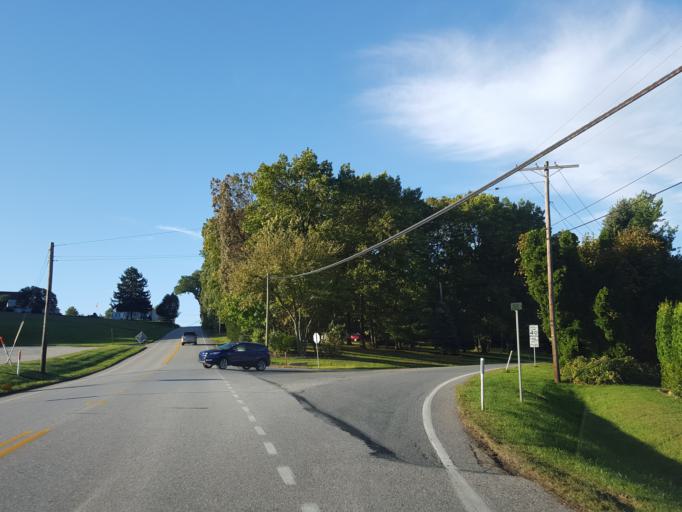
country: US
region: Pennsylvania
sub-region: York County
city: Windsor
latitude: 39.9252
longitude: -76.6068
